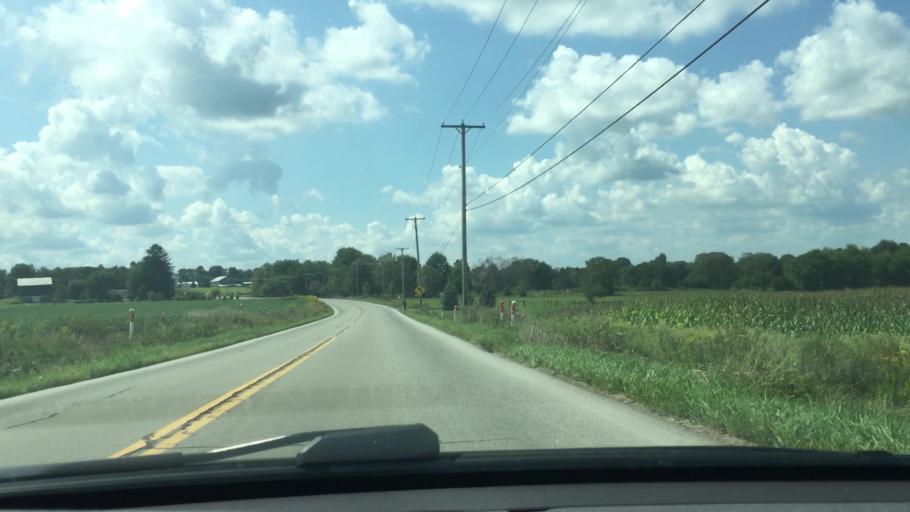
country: US
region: Pennsylvania
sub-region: Lawrence County
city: New Wilmington
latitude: 41.1205
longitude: -80.4004
